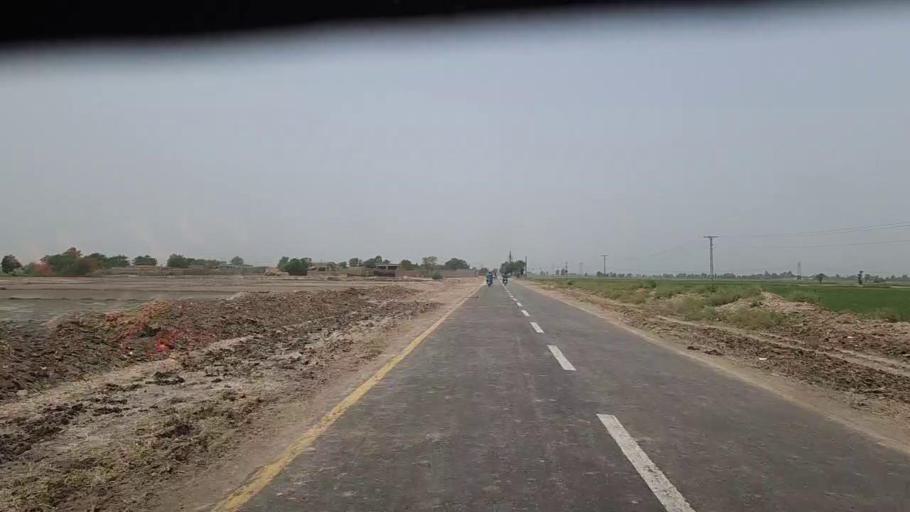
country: PK
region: Sindh
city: Sita Road
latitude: 27.0404
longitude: 67.8859
